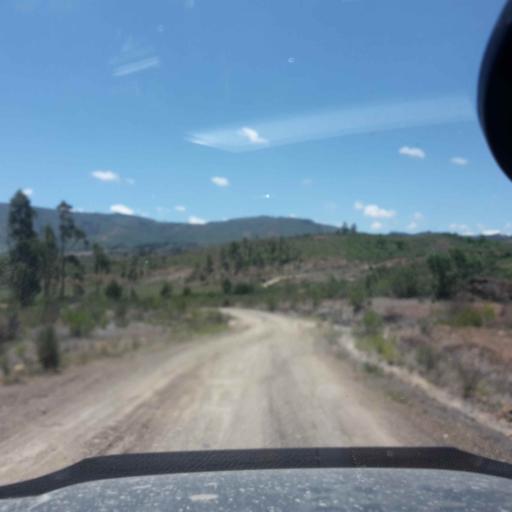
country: BO
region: Cochabamba
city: Totora
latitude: -17.7707
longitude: -65.2642
